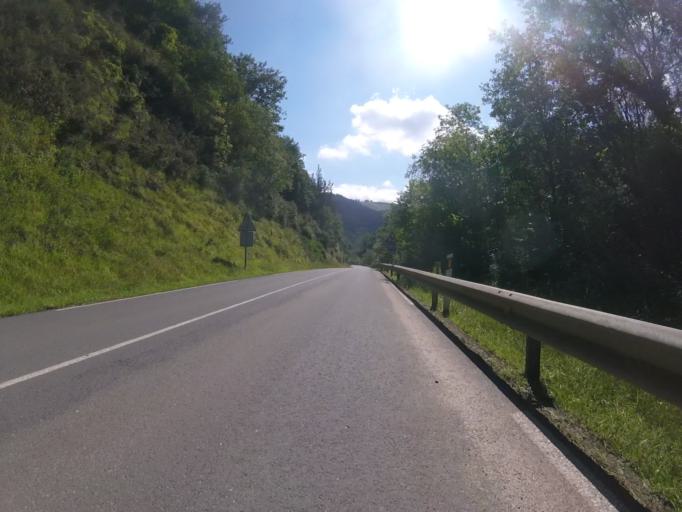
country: ES
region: Basque Country
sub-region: Provincia de Guipuzcoa
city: Beizama
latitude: 43.1136
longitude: -2.2307
